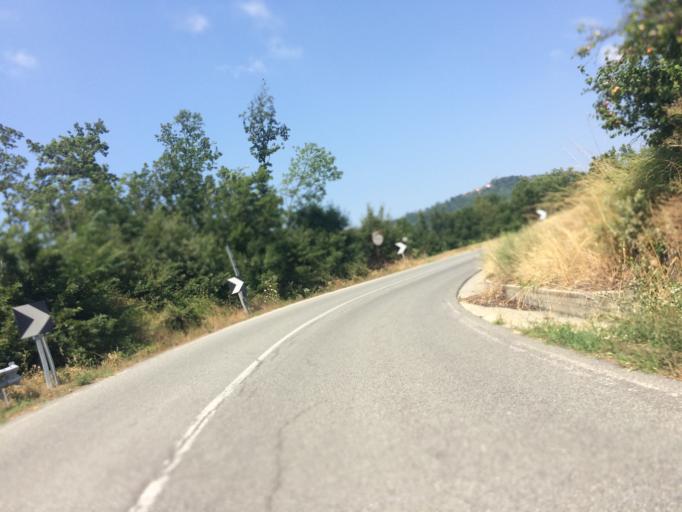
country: IT
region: Piedmont
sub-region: Provincia di Alessandria
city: Castelletto d'Erro
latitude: 44.6131
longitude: 8.4133
